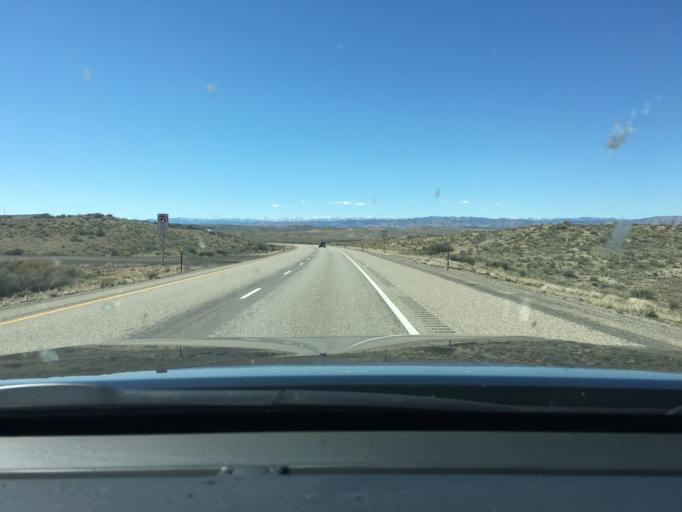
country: US
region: Colorado
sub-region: Mesa County
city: Loma
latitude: 39.1954
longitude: -109.0579
